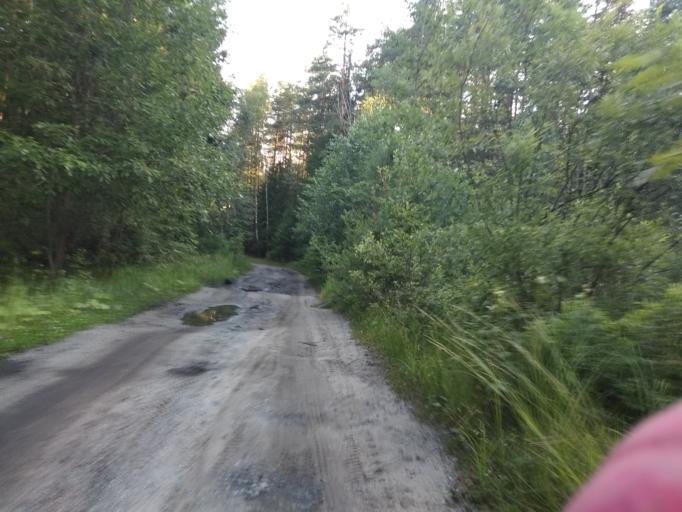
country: RU
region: Moskovskaya
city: Misheronskiy
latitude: 55.7267
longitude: 39.7543
